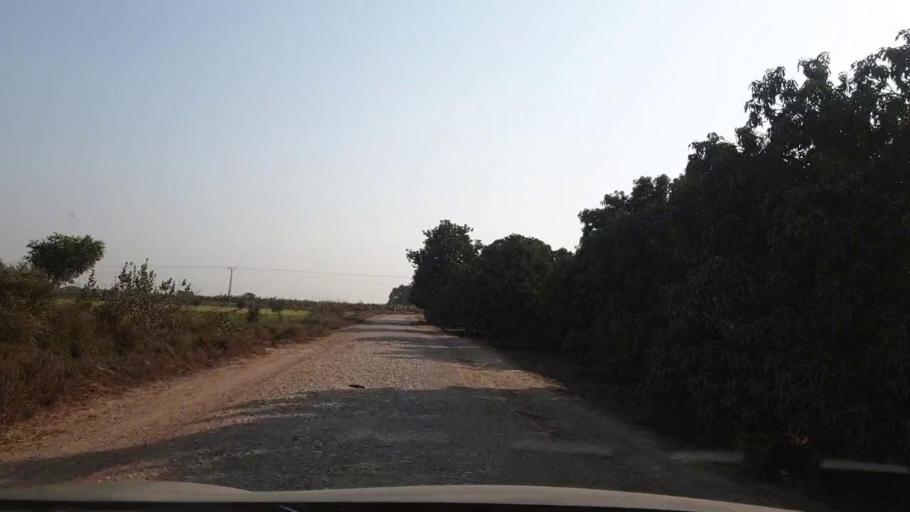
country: PK
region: Sindh
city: Tando Allahyar
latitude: 25.5654
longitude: 68.7641
